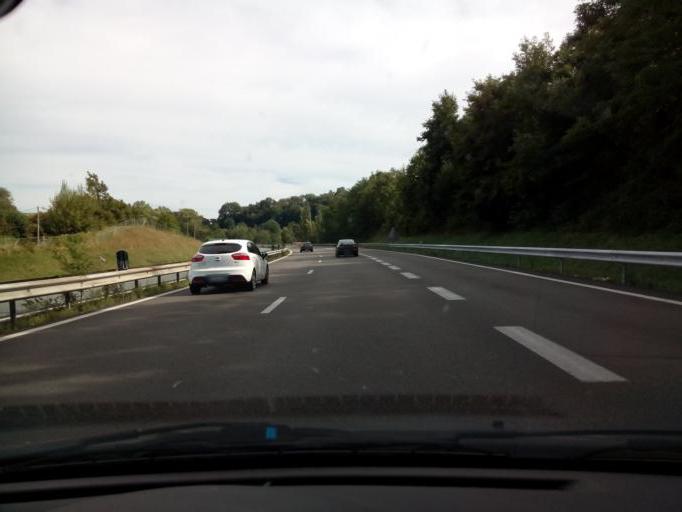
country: FR
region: Rhone-Alpes
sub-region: Departement de l'Isere
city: Cessieu
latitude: 45.5459
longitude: 5.3747
